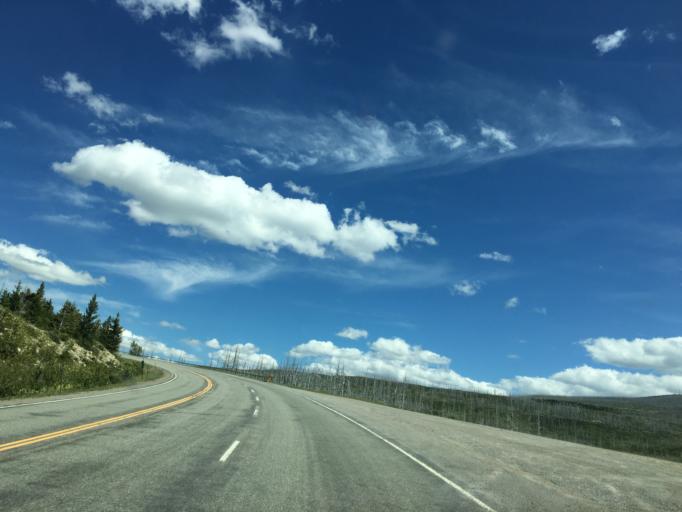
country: US
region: Montana
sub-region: Glacier County
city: North Browning
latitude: 48.7011
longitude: -113.4128
